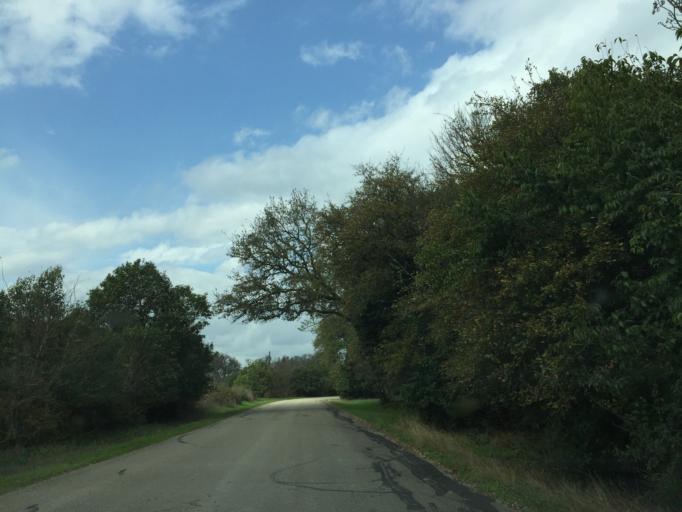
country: US
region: Texas
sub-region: Travis County
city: Manchaca
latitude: 30.1411
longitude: -97.8233
